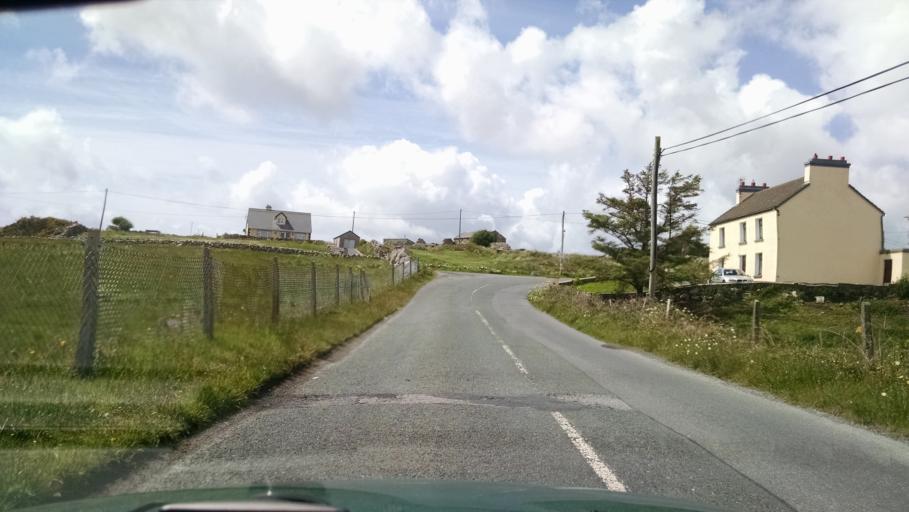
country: IE
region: Connaught
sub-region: County Galway
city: Clifden
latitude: 53.3062
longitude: -9.7803
